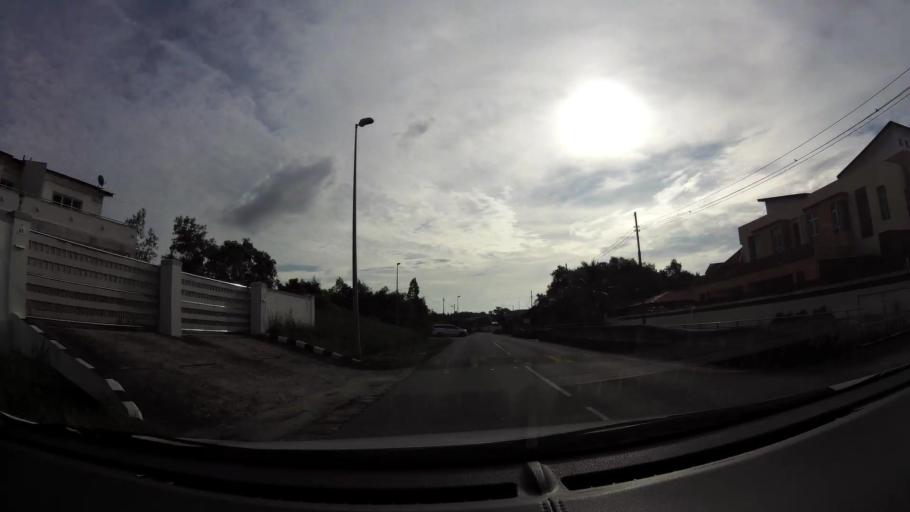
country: BN
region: Brunei and Muara
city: Bandar Seri Begawan
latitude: 4.9054
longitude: 114.8964
